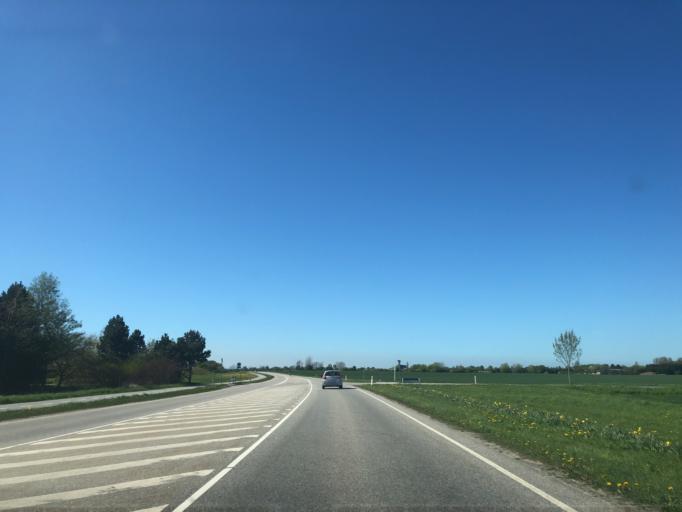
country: DK
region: Zealand
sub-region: Stevns Kommune
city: Store Heddinge
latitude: 55.3494
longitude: 12.3330
